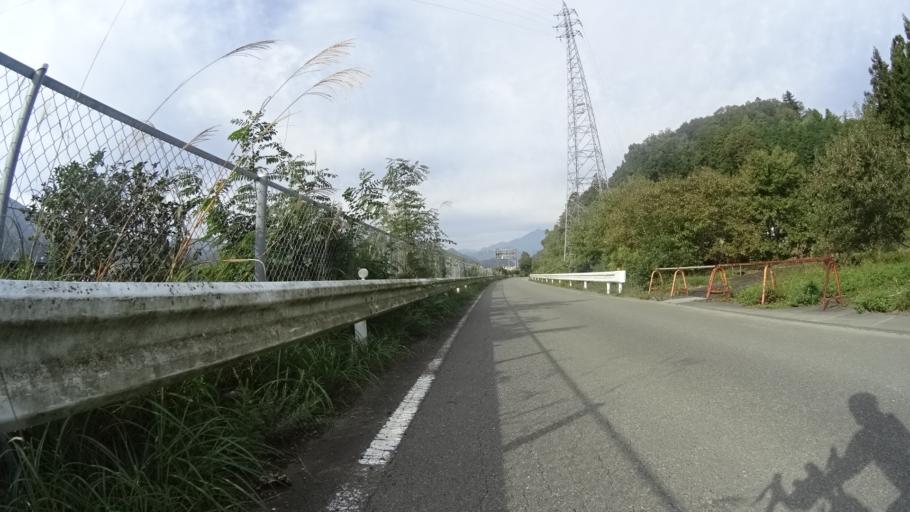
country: JP
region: Yamanashi
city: Otsuki
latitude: 35.6104
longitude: 139.0105
